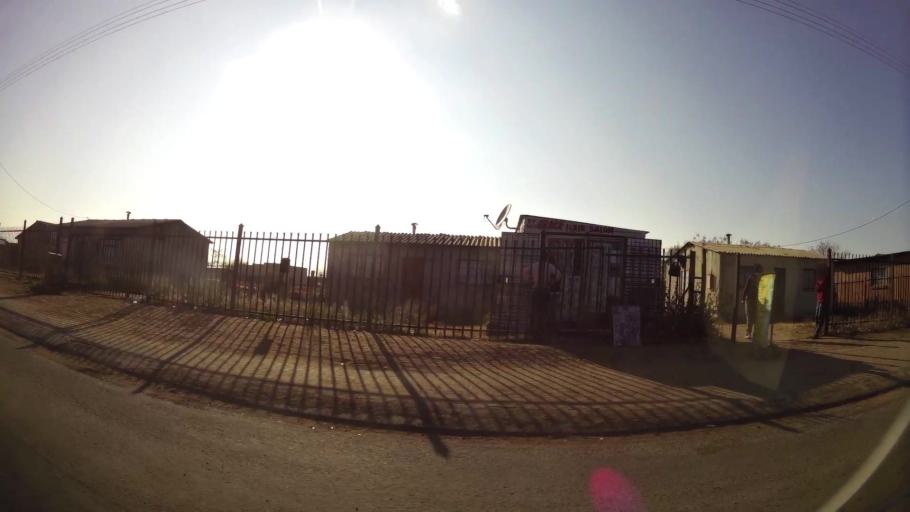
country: ZA
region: Orange Free State
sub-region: Mangaung Metropolitan Municipality
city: Bloemfontein
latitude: -29.1537
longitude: 26.2530
